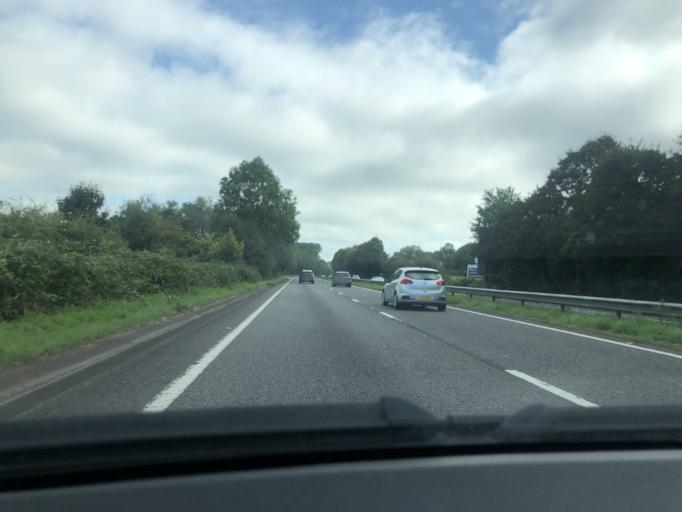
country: GB
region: England
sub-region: Devon
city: Honiton
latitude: 50.7982
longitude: -3.2057
